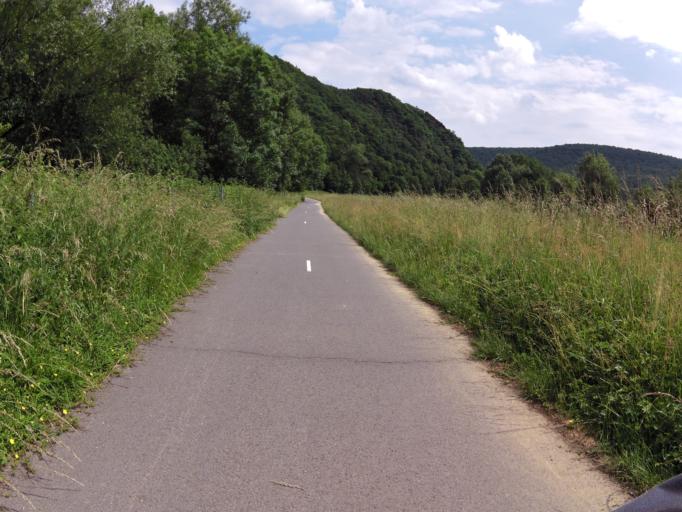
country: FR
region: Champagne-Ardenne
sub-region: Departement des Ardennes
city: Nouzonville
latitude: 49.8390
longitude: 4.7667
